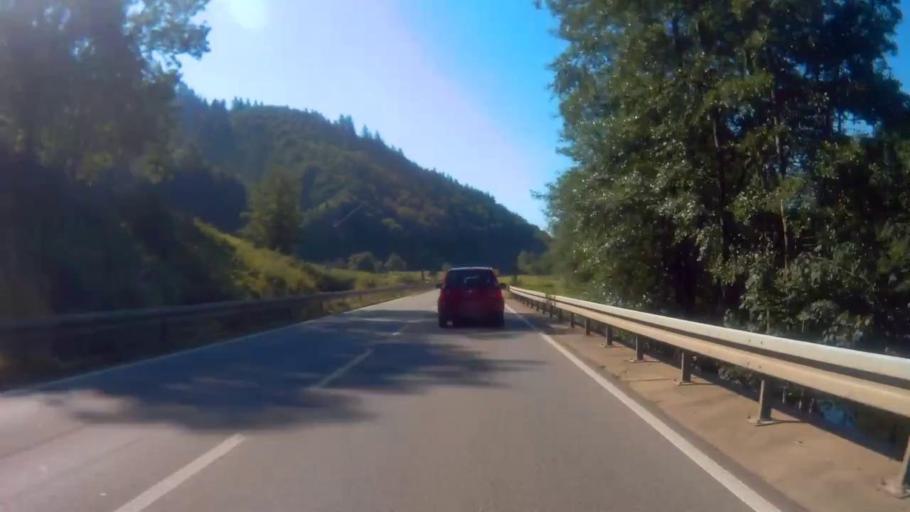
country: DE
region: Baden-Wuerttemberg
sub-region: Freiburg Region
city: Hausen
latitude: 47.6905
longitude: 7.8440
